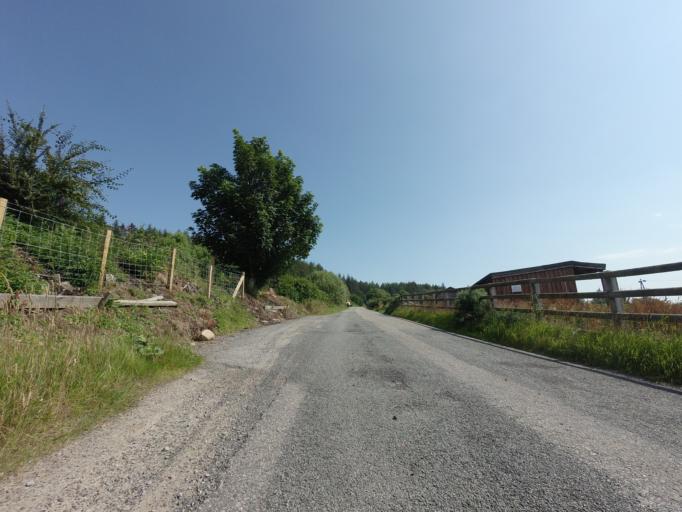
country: GB
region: Scotland
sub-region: Highland
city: Invergordon
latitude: 57.7577
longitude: -4.1325
